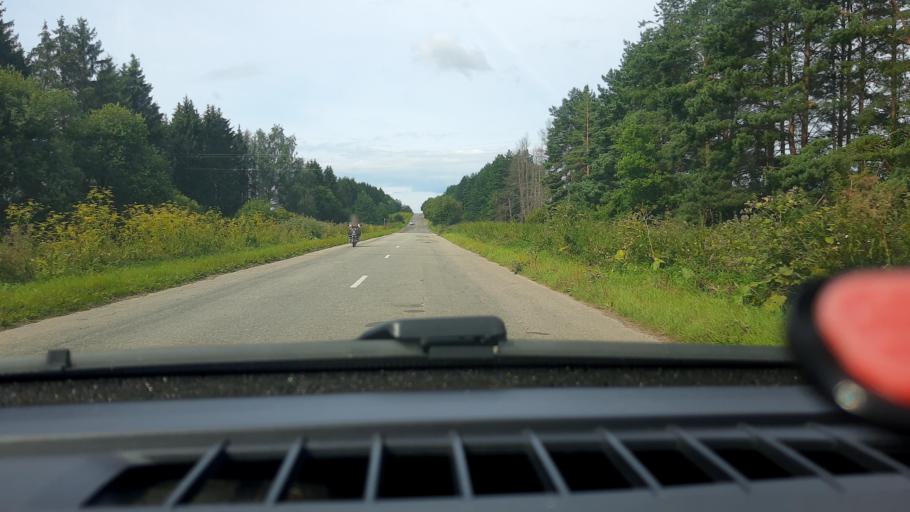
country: RU
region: Nizjnij Novgorod
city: Bogorodsk
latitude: 56.0670
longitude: 43.6452
